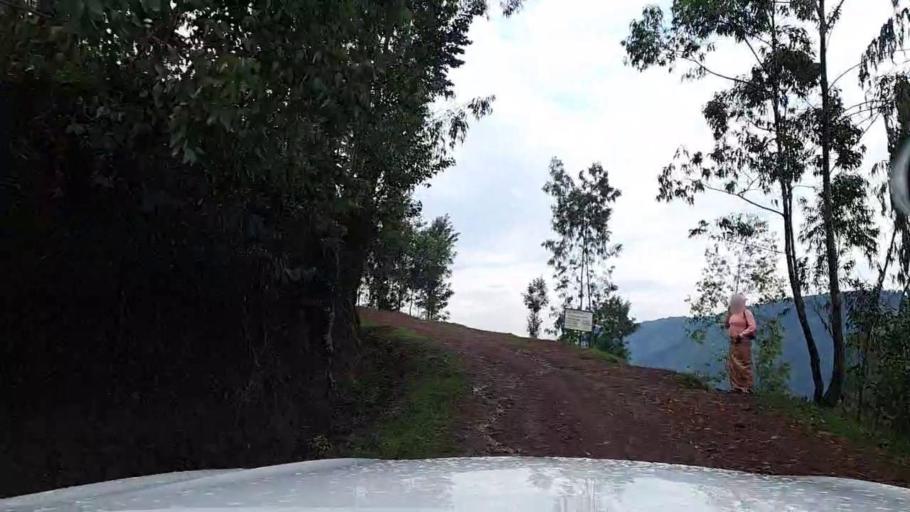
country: RW
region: Northern Province
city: Byumba
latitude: -1.7207
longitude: 29.9171
